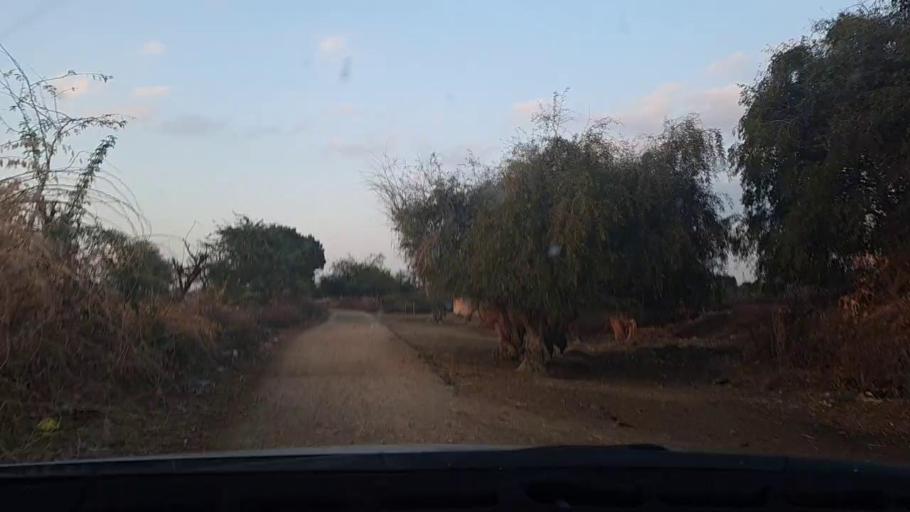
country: PK
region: Sindh
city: Tando Mittha Khan
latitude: 25.9450
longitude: 69.3383
